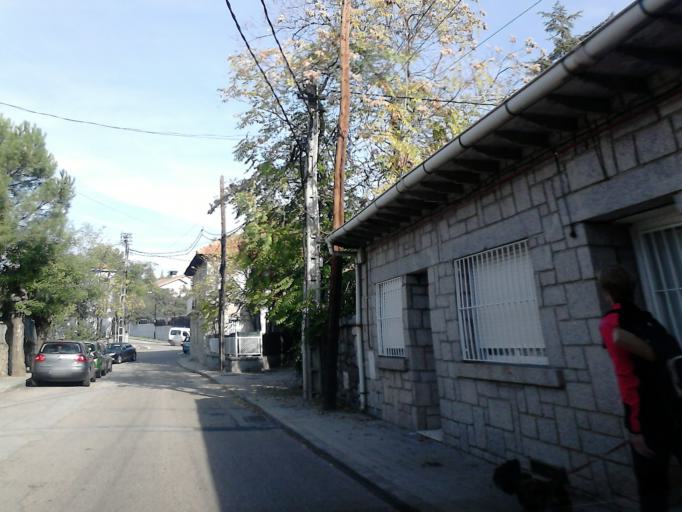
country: ES
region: Madrid
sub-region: Provincia de Madrid
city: Torrelodones
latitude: 40.5791
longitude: -3.9593
